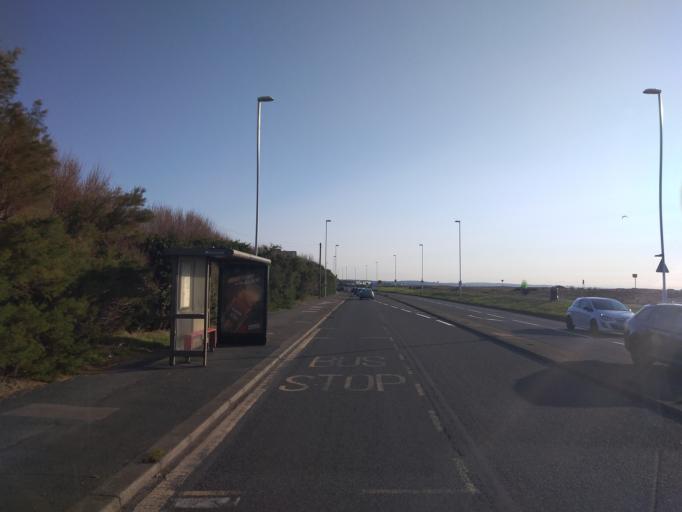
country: GB
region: England
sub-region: West Sussex
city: Lancing
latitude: 50.8165
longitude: -0.3374
